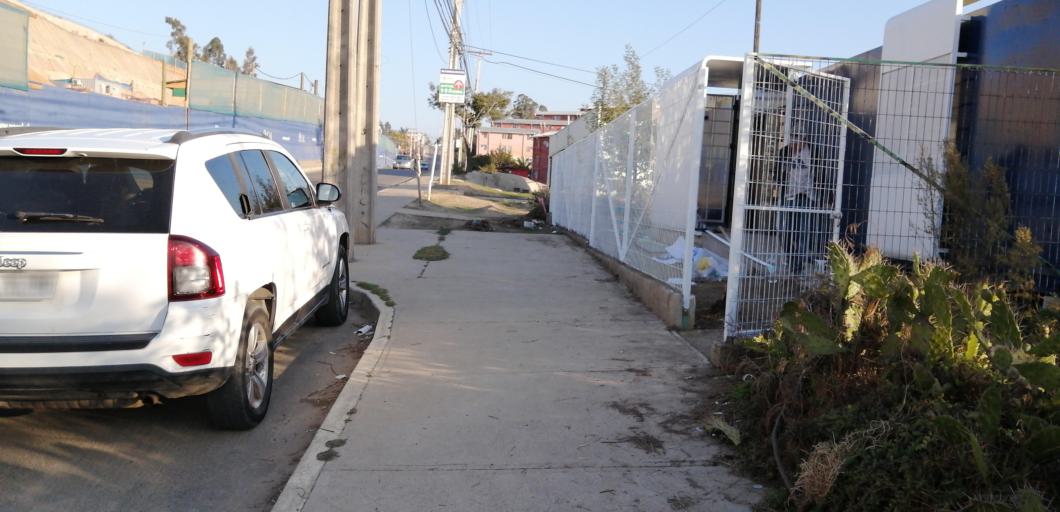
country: CL
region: Valparaiso
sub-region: Provincia de Marga Marga
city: Quilpue
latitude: -33.0569
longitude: -71.4411
